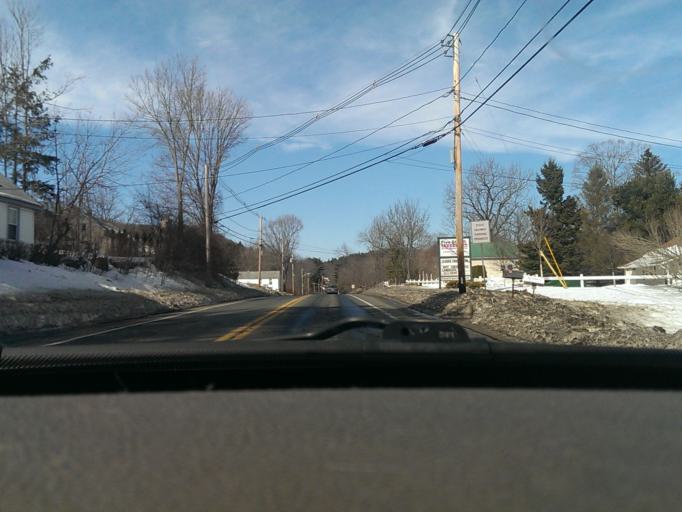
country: US
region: Massachusetts
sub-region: Hampden County
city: Palmer
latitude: 42.1831
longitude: -72.3147
